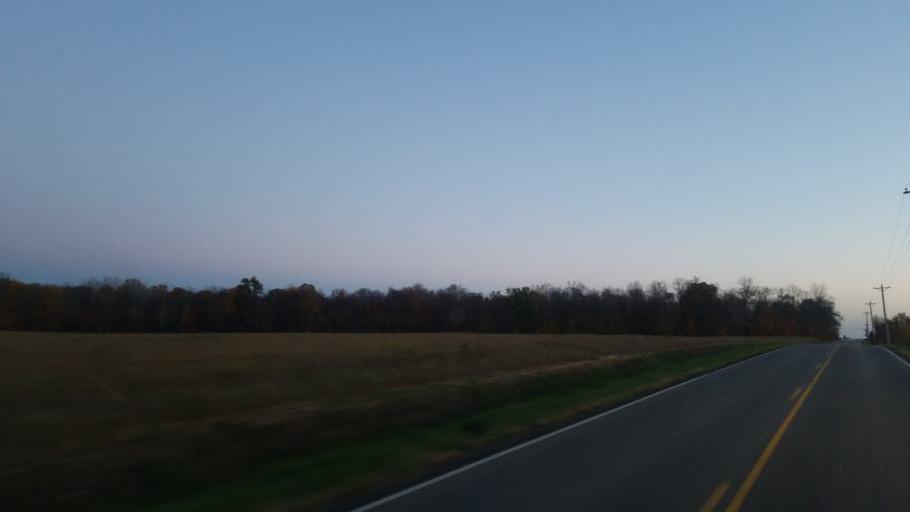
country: US
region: Ohio
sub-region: Richland County
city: Shelby
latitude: 40.9186
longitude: -82.7434
